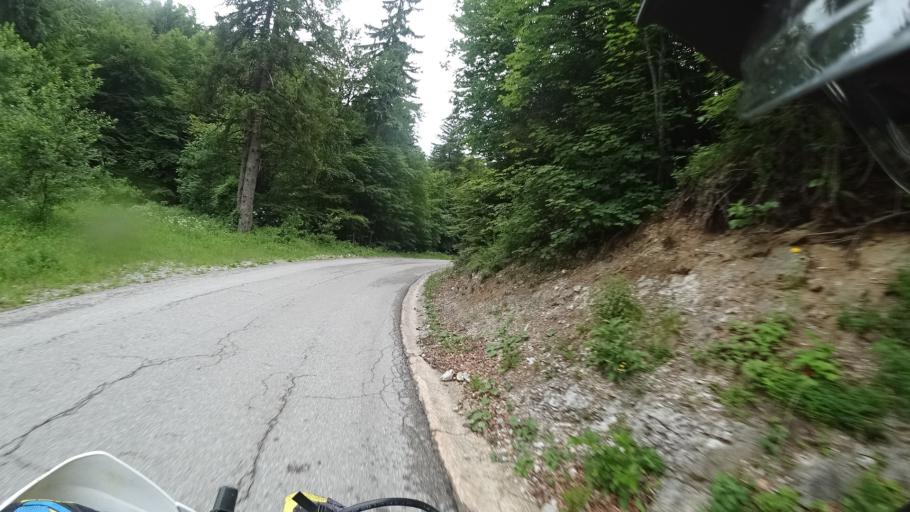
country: HR
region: Primorsko-Goranska
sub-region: Grad Delnice
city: Delnice
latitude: 45.3947
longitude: 14.8175
